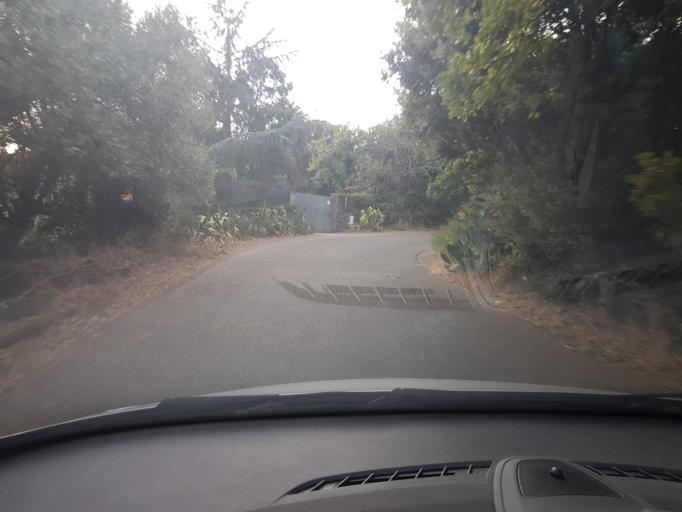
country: IT
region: Sardinia
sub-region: Provincia di Oristano
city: Seneghe
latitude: 40.0885
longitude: 8.6189
